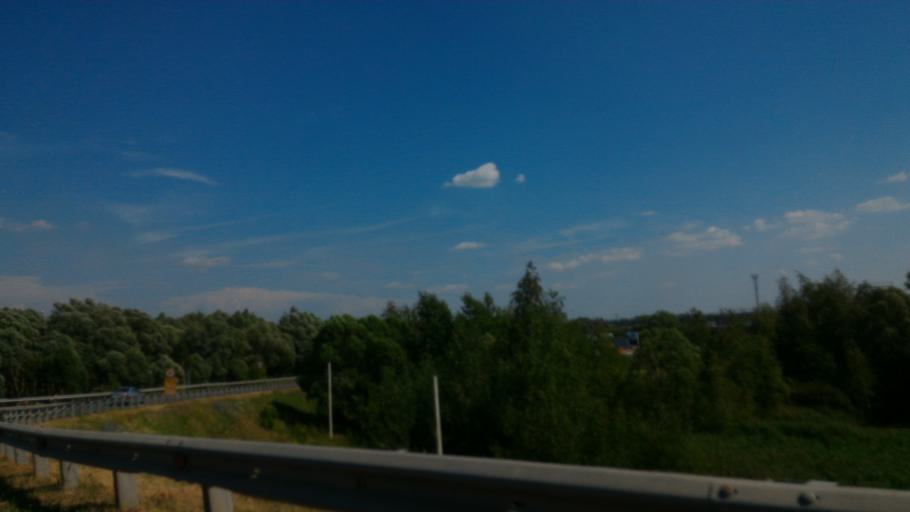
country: RU
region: Rjazan
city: Rybnoye
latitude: 54.7407
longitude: 39.4860
